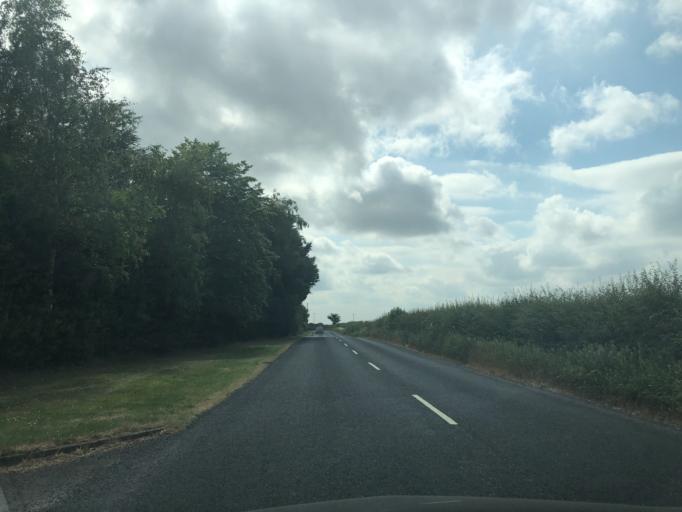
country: GB
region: England
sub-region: North Yorkshire
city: Stokesley
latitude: 54.4597
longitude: -1.2414
